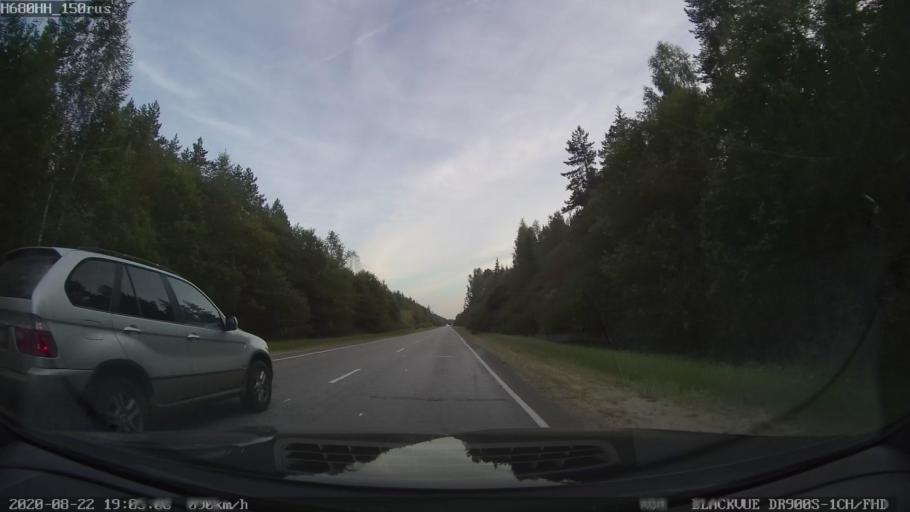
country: RU
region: Tverskaya
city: Sakharovo
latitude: 57.0809
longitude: 36.1132
